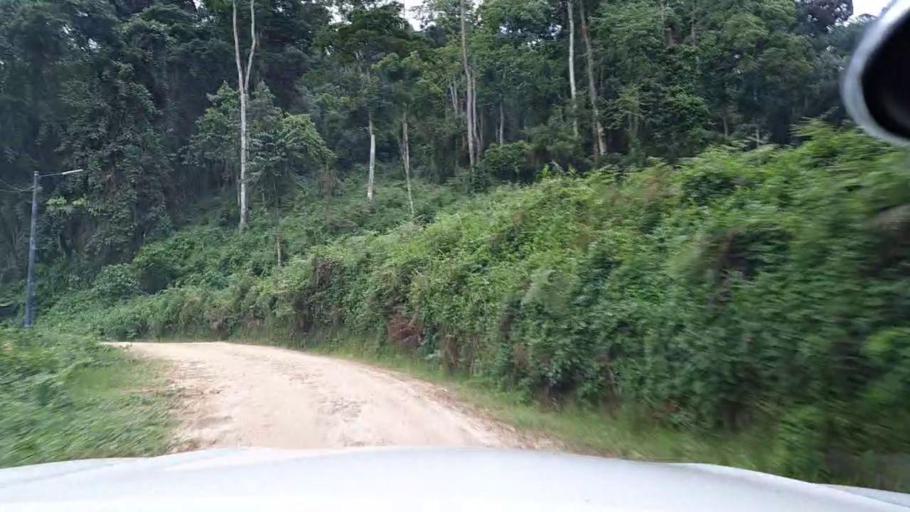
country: RW
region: Western Province
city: Cyangugu
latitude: -2.5677
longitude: 29.2304
